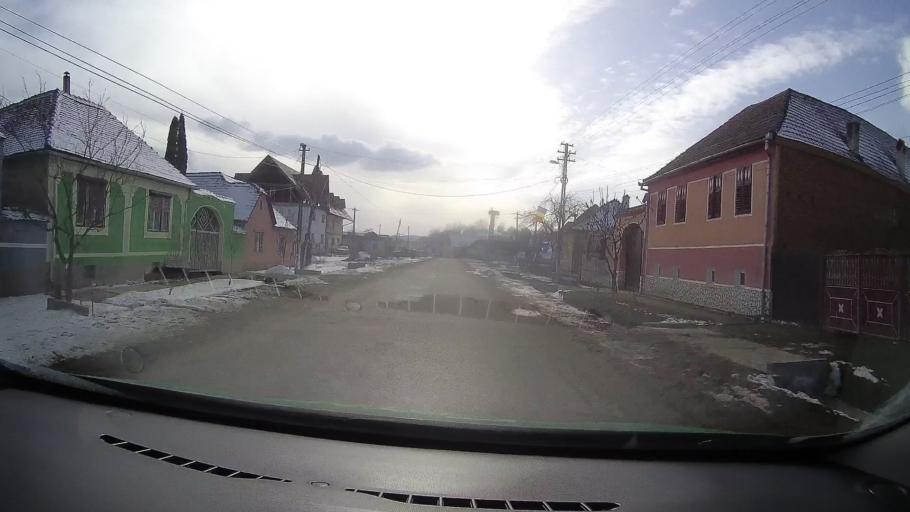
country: RO
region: Sibiu
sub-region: Comuna Bradeni
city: Bradeni
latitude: 46.0578
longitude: 24.7862
